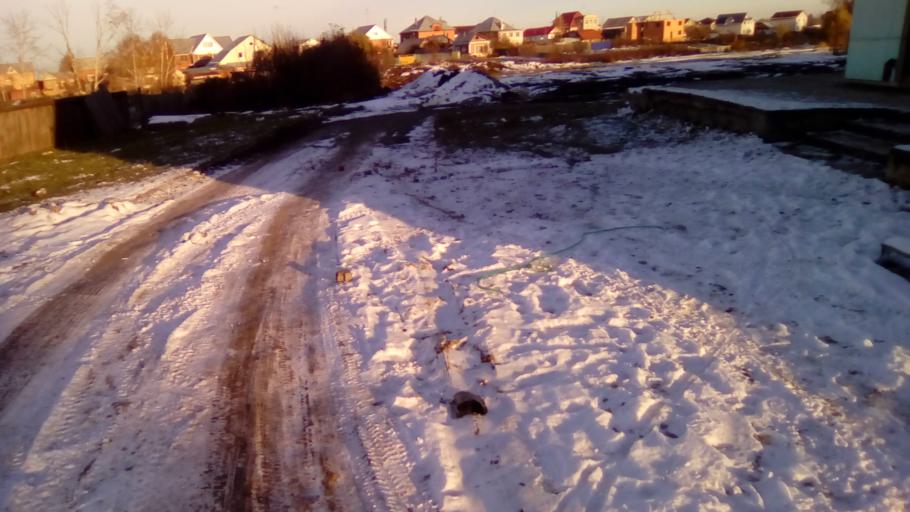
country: RU
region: Tjumen
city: Moskovskiy
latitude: 57.2219
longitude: 65.3598
